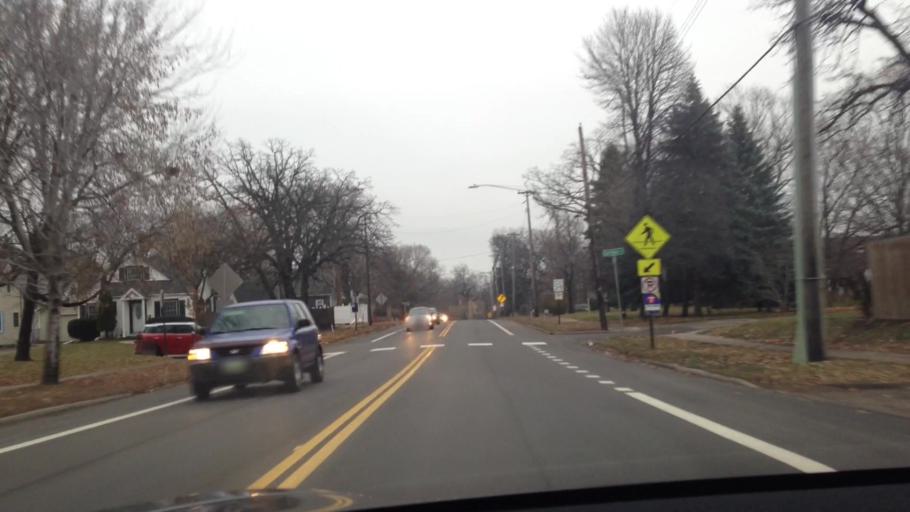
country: US
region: Minnesota
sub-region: Hennepin County
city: Saint Louis Park
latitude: 44.9495
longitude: -93.3550
